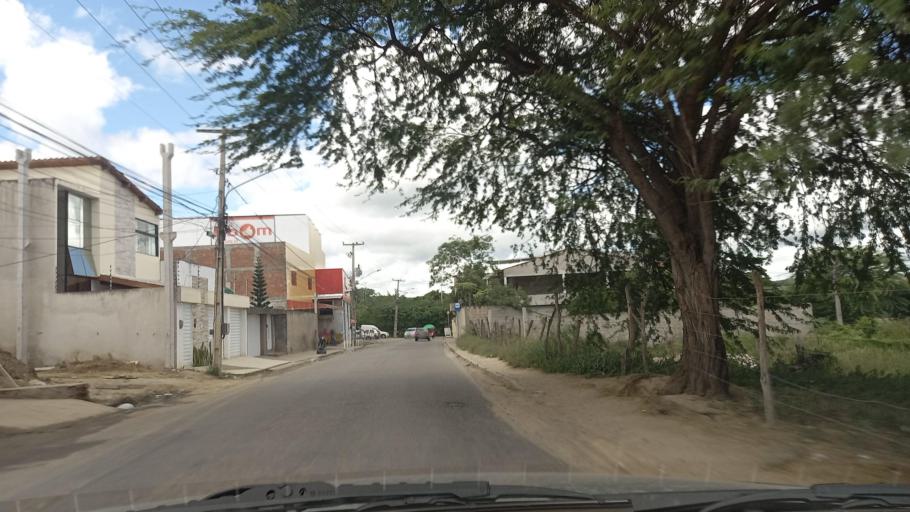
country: BR
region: Pernambuco
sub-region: Caruaru
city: Caruaru
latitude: -8.2786
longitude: -35.9405
